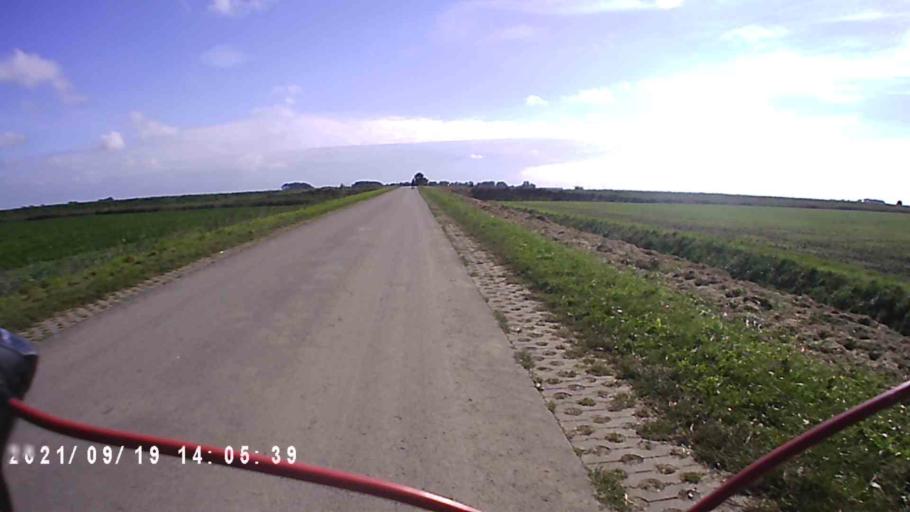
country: NL
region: Groningen
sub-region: Gemeente  Oldambt
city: Winschoten
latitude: 53.1438
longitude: 7.1234
